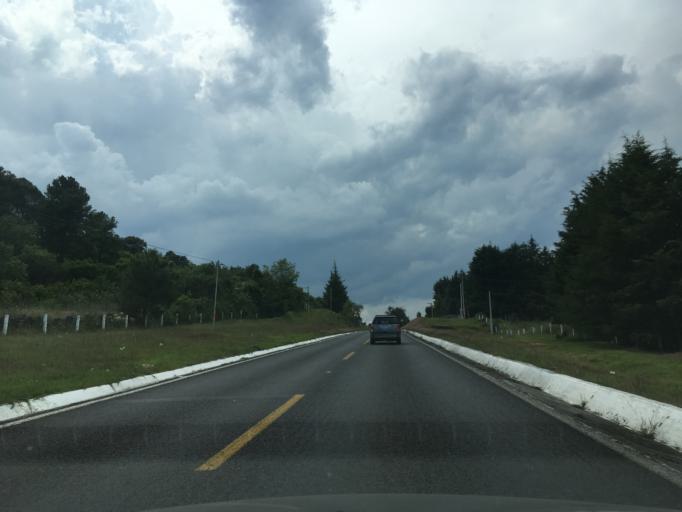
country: MX
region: Michoacan
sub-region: Patzcuaro
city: Santa Ana Chapitiro
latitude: 19.5227
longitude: -101.6554
